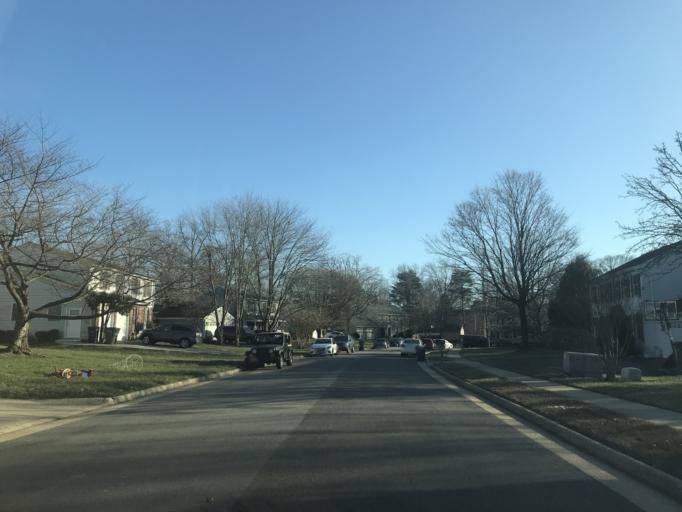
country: US
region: Virginia
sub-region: Fairfax County
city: Franconia
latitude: 38.7874
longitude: -77.1484
